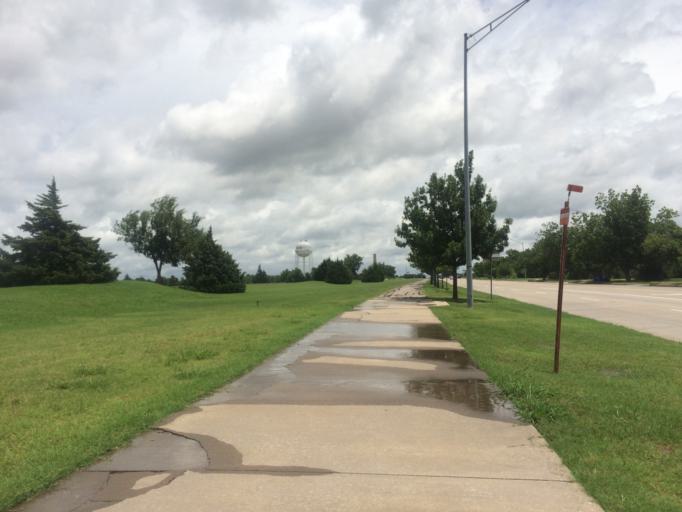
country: US
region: Oklahoma
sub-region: Cleveland County
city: Norman
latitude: 35.2331
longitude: -97.4588
